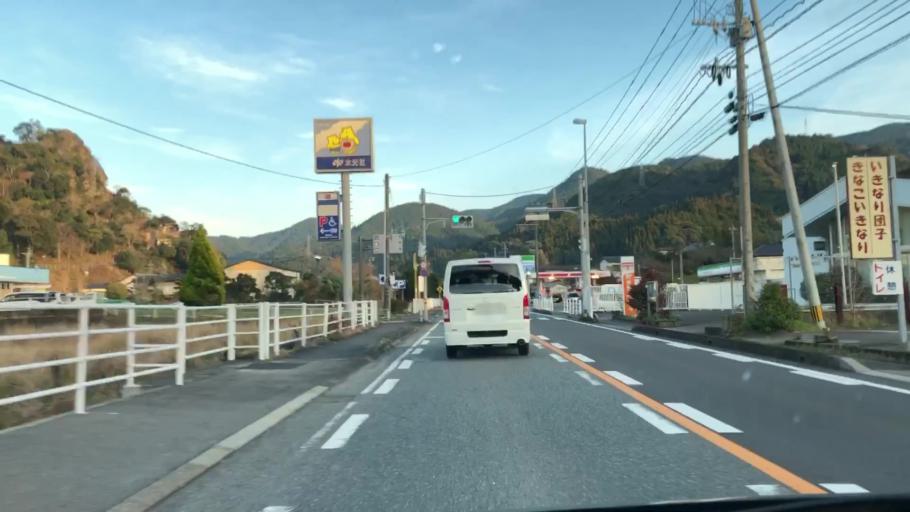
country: JP
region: Kumamoto
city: Minamata
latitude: 32.2325
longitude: 130.4531
